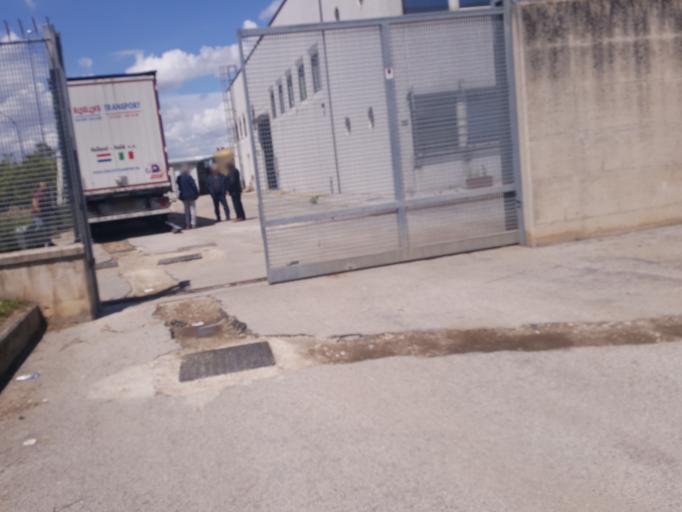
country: IT
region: Campania
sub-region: Provincia di Napoli
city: Pascarola
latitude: 40.9852
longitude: 14.2950
